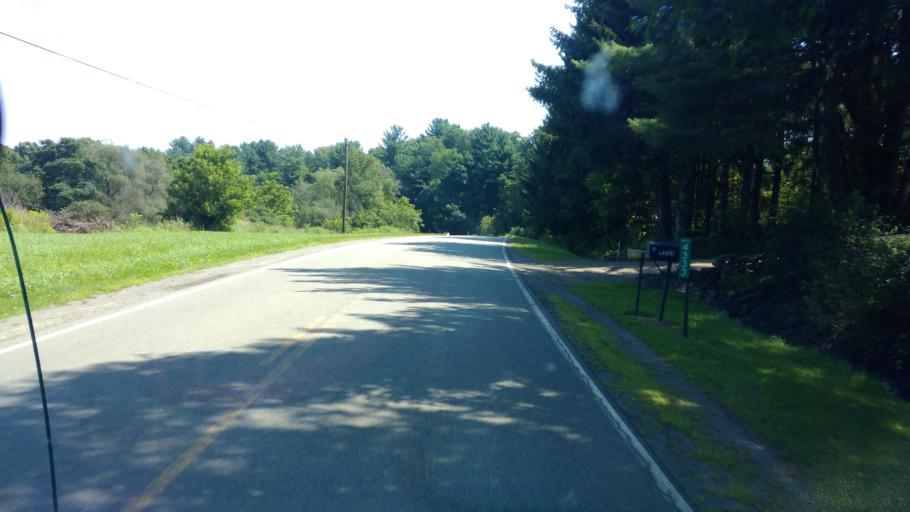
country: US
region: New York
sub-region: Allegany County
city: Belmont
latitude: 42.2983
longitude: -77.9761
